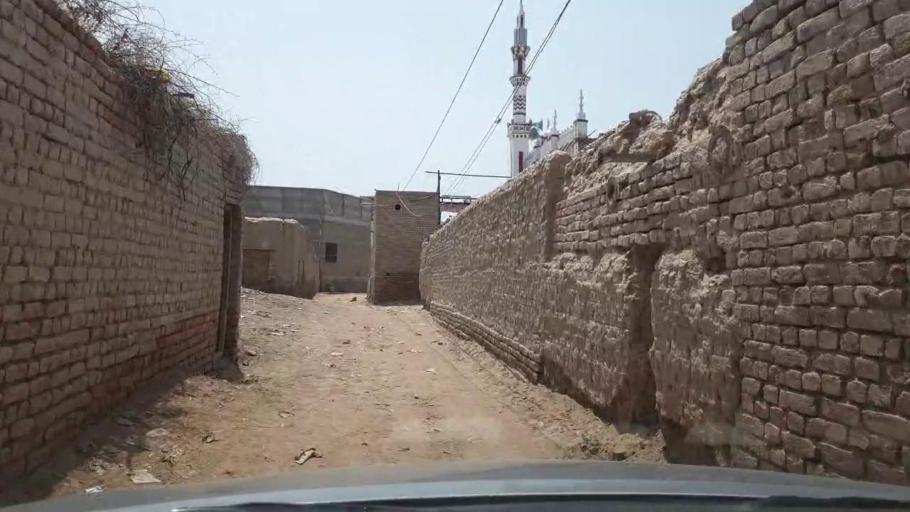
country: PK
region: Sindh
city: Madeji
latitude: 27.7606
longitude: 68.3830
